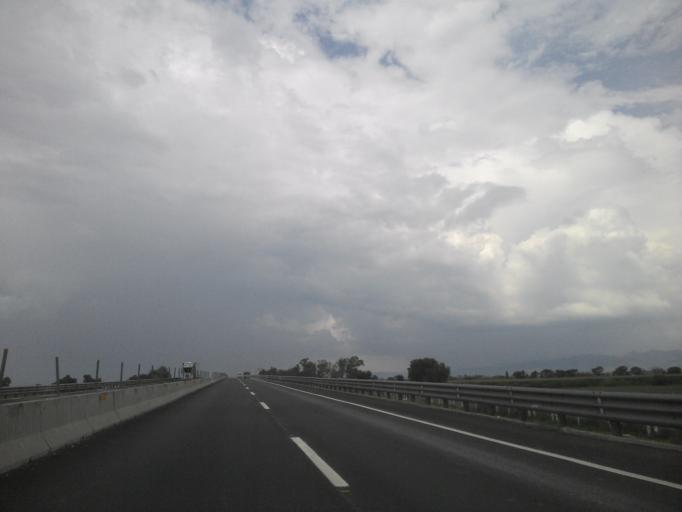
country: MX
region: Hidalgo
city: El Llano
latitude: 20.0860
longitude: -99.3233
